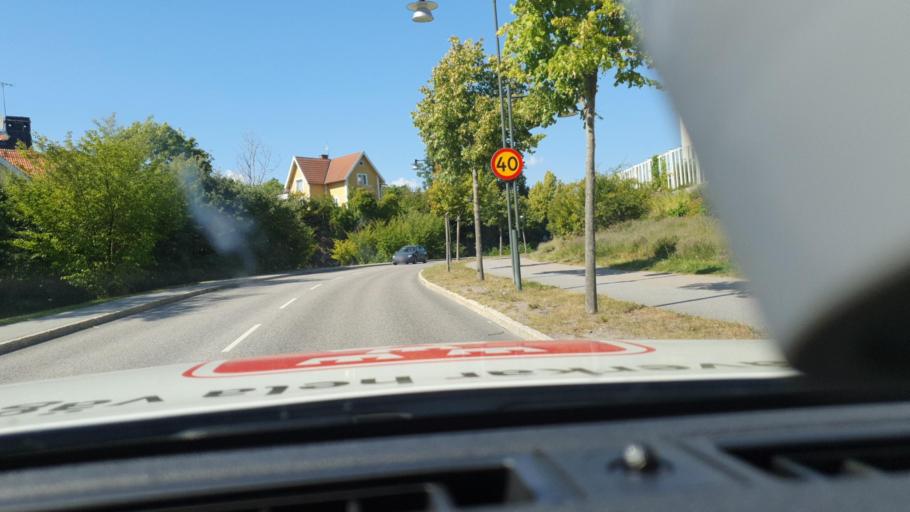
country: SE
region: Stockholm
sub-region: Norrtalje Kommun
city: Bergshamra
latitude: 59.3829
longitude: 18.0491
